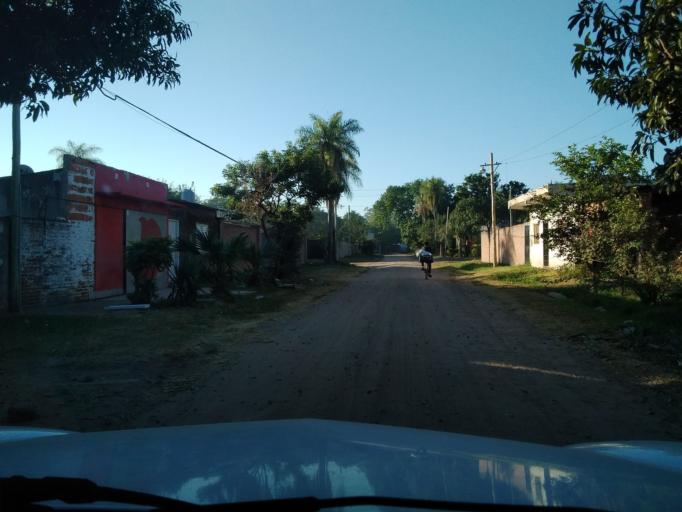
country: AR
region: Corrientes
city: Corrientes
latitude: -27.4789
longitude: -58.7859
